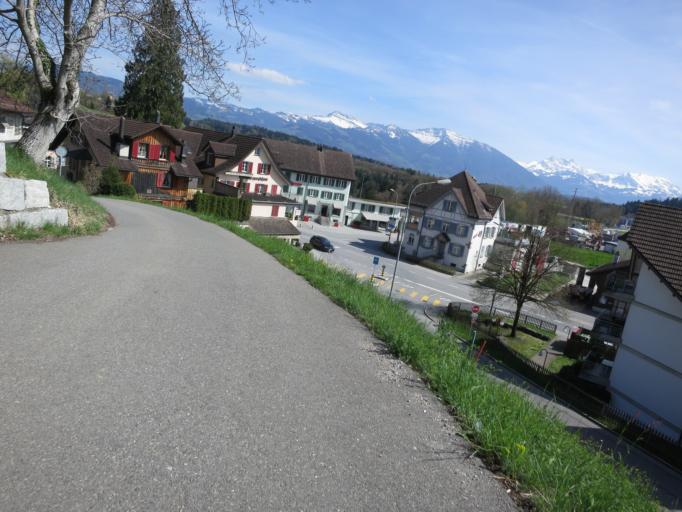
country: CH
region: Saint Gallen
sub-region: Wahlkreis See-Gaster
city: Schmerikon
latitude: 47.2433
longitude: 8.9464
